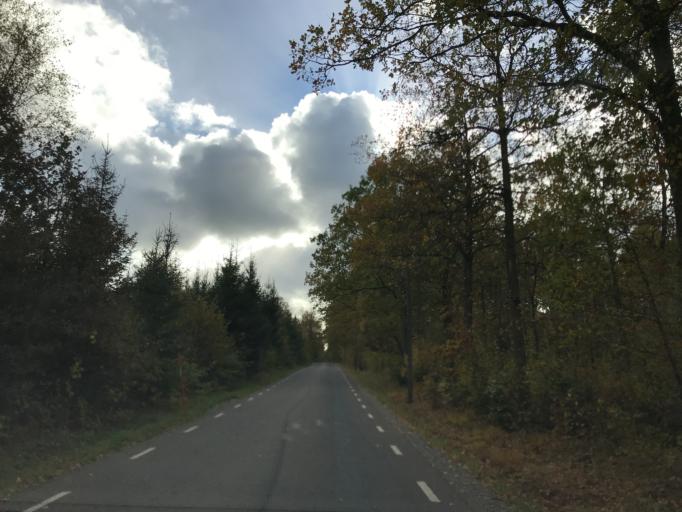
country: SE
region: Skane
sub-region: Bjuvs Kommun
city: Billesholm
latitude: 56.0282
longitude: 13.0062
